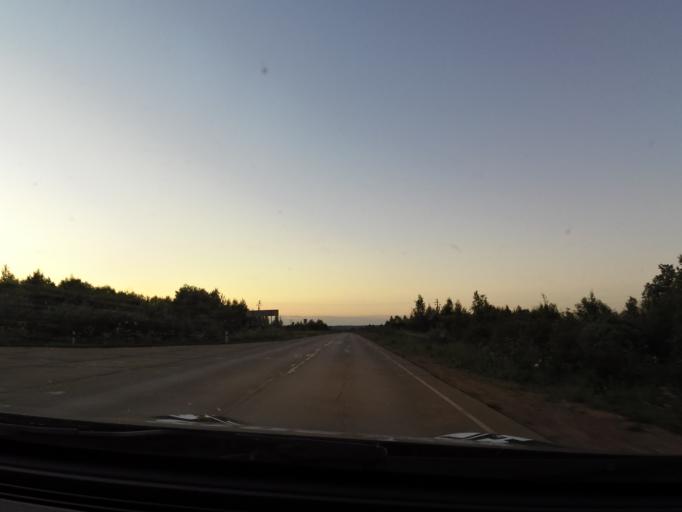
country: RU
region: Vologda
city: Vytegra
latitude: 60.8860
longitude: 36.0407
